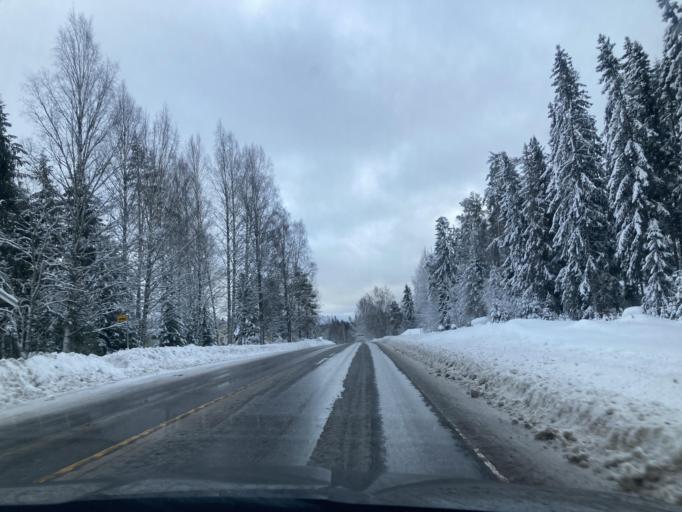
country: FI
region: Paijanne Tavastia
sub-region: Lahti
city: Padasjoki
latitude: 61.3269
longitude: 25.2742
